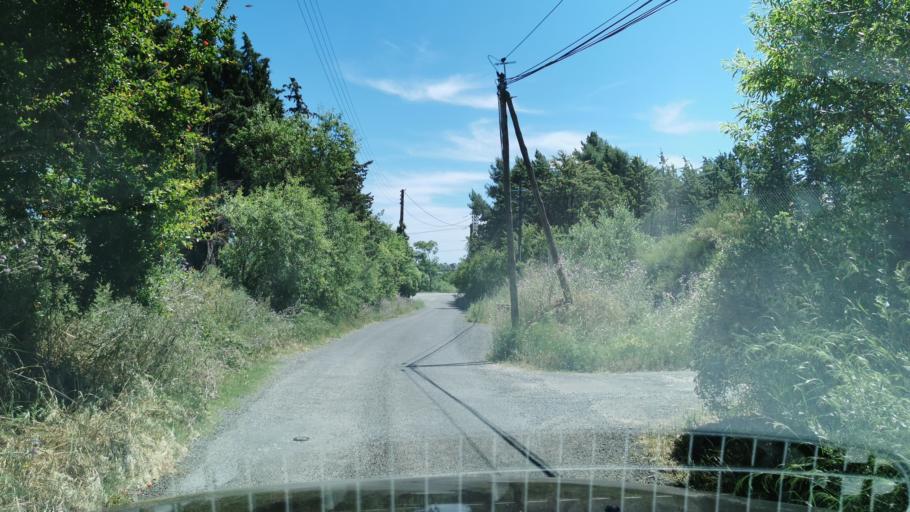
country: FR
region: Languedoc-Roussillon
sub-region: Departement de l'Aude
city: Narbonne
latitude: 43.2003
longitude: 2.9797
